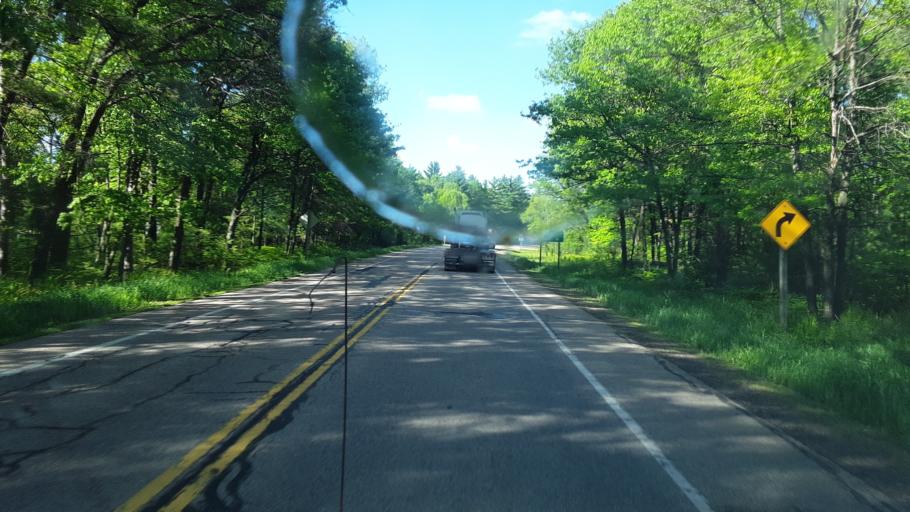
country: US
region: Wisconsin
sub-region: Wood County
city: Nekoosa
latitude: 44.2964
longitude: -90.1261
